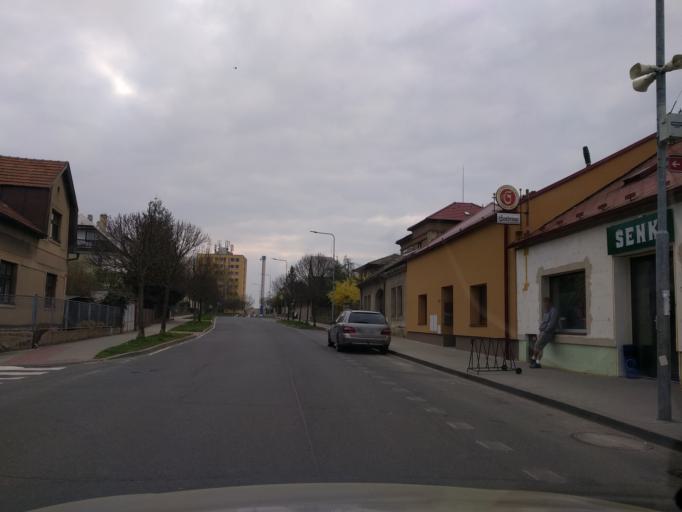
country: CZ
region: Central Bohemia
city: Cesky Brod
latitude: 50.0705
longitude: 14.8534
